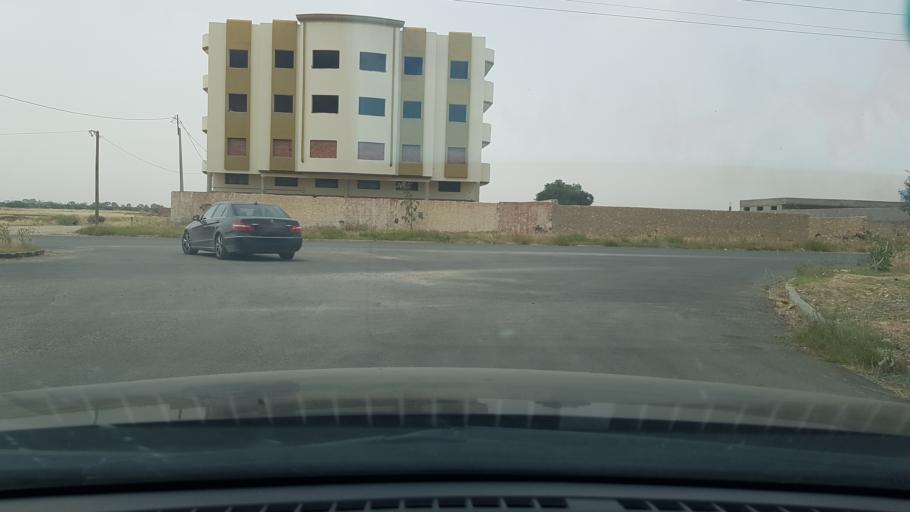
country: TN
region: Safaqis
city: Al Qarmadah
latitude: 34.8275
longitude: 10.7396
